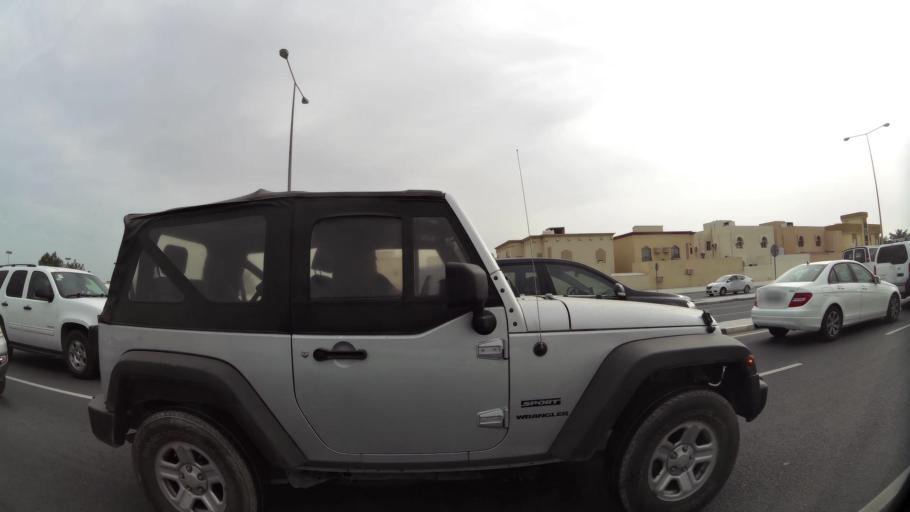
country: QA
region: Baladiyat ad Dawhah
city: Doha
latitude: 25.3353
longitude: 51.4841
